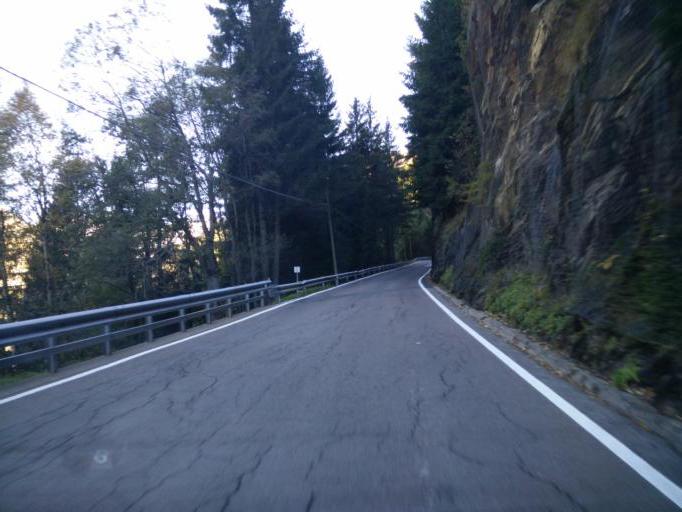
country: IT
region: Trentino-Alto Adige
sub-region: Bolzano
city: Moso in Passiria
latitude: 46.8412
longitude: 11.1677
